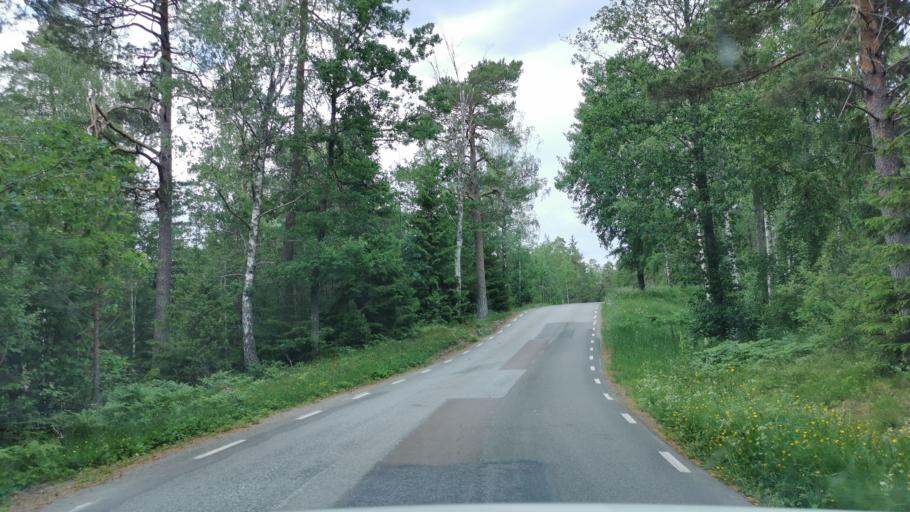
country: SE
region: Vaestra Goetaland
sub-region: Bengtsfors Kommun
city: Dals Langed
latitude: 58.8688
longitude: 12.4020
